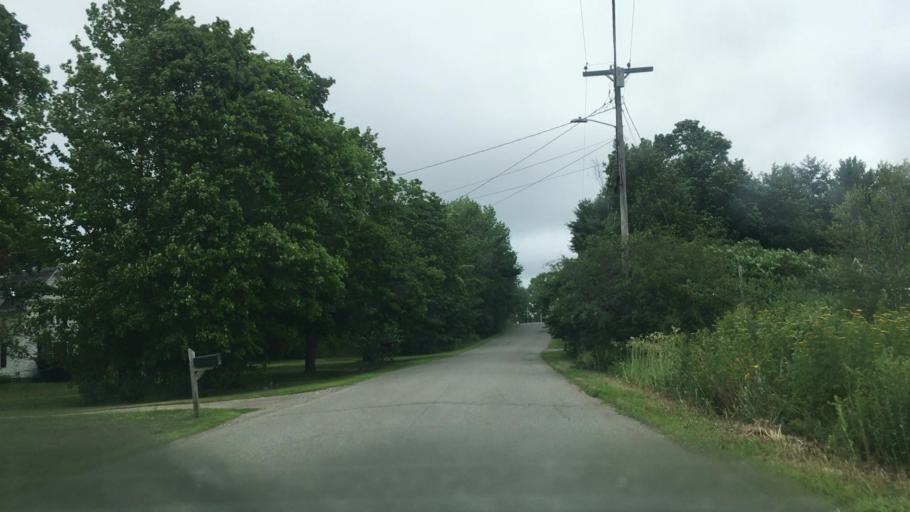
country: US
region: Maine
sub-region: Penobscot County
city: Veazie
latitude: 44.8445
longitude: -68.7462
